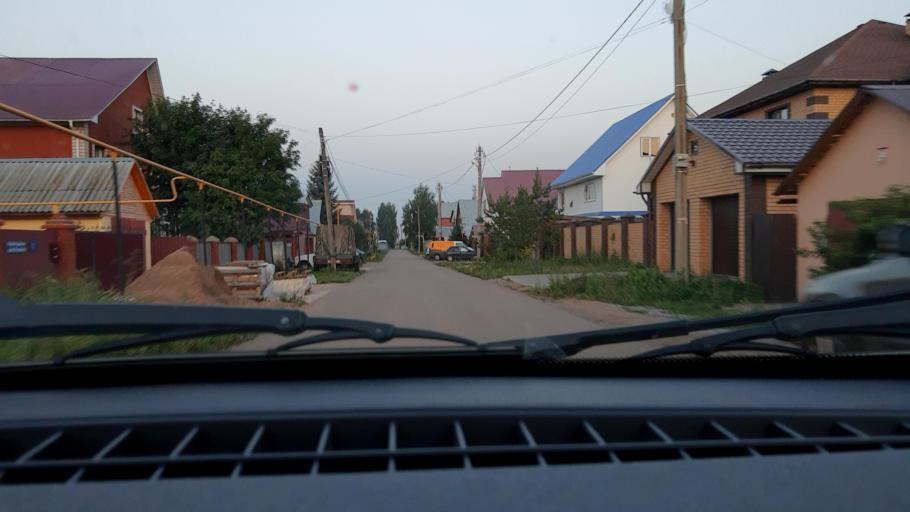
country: RU
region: Bashkortostan
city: Mikhaylovka
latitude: 54.8103
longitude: 55.7861
